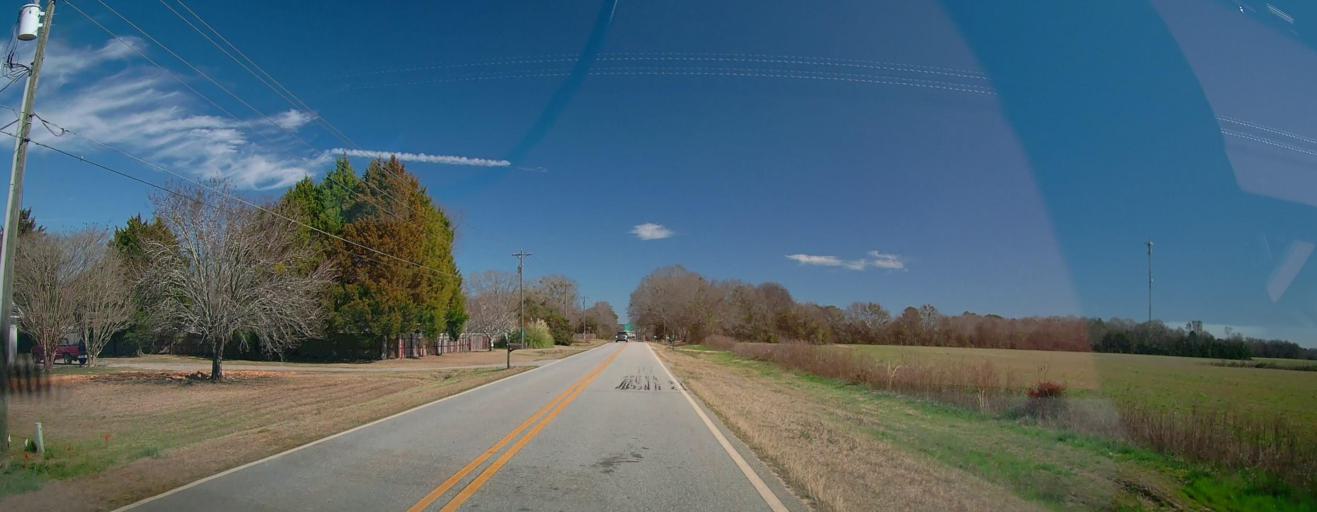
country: US
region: Georgia
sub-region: Houston County
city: Perry
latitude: 32.4851
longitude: -83.6230
